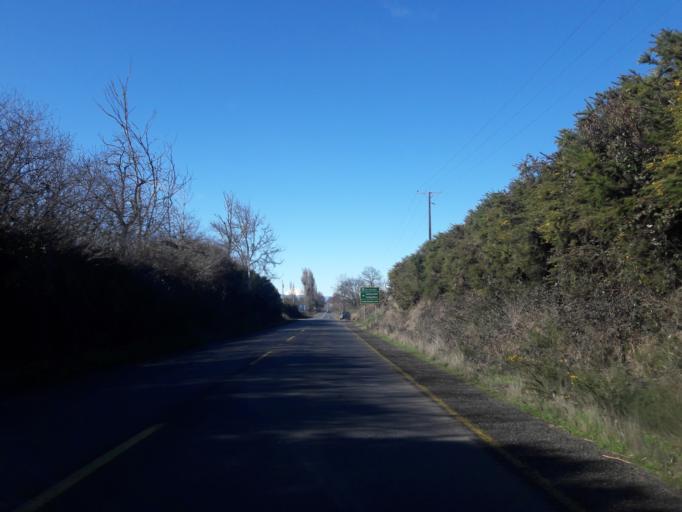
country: CL
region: Araucania
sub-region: Provincia de Malleco
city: Victoria
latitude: -38.2576
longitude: -72.2641
